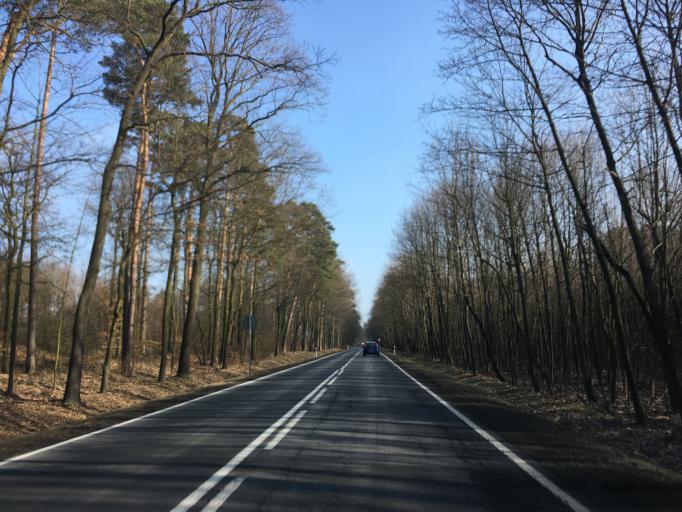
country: PL
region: Lower Silesian Voivodeship
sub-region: Powiat legnicki
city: Chojnow
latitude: 51.2747
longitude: 15.8785
